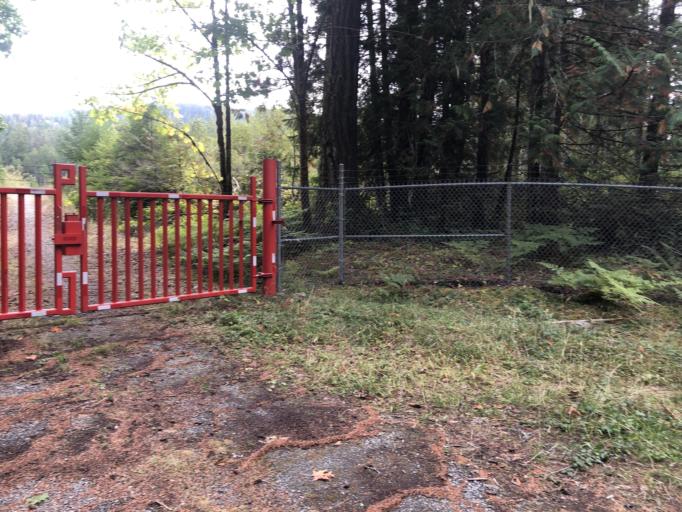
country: CA
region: British Columbia
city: Sooke
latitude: 48.4950
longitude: -123.7100
